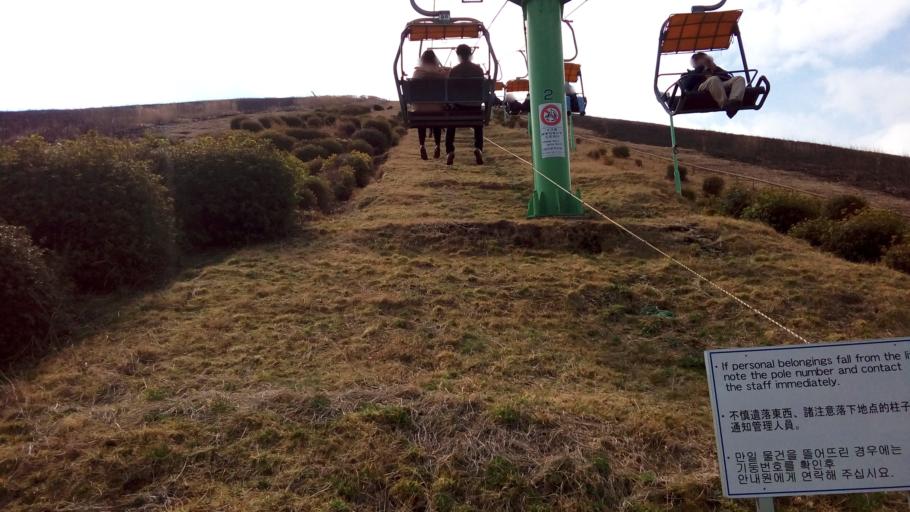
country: JP
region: Shizuoka
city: Ito
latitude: 34.9074
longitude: 139.0966
